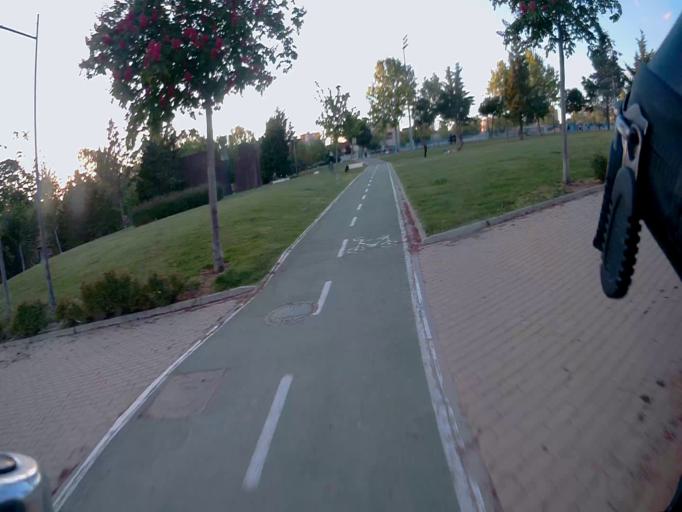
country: ES
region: Madrid
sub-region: Provincia de Madrid
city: Alcorcon
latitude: 40.3363
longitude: -3.8241
